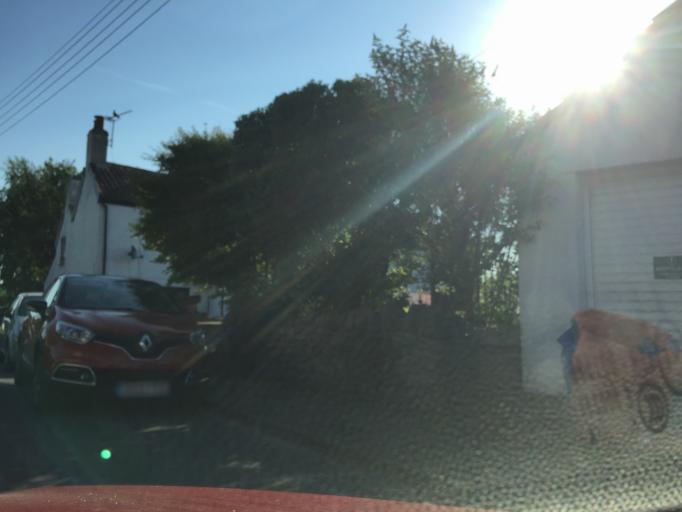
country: GB
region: England
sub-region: South Gloucestershire
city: Winterbourne
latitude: 51.5276
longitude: -2.4945
